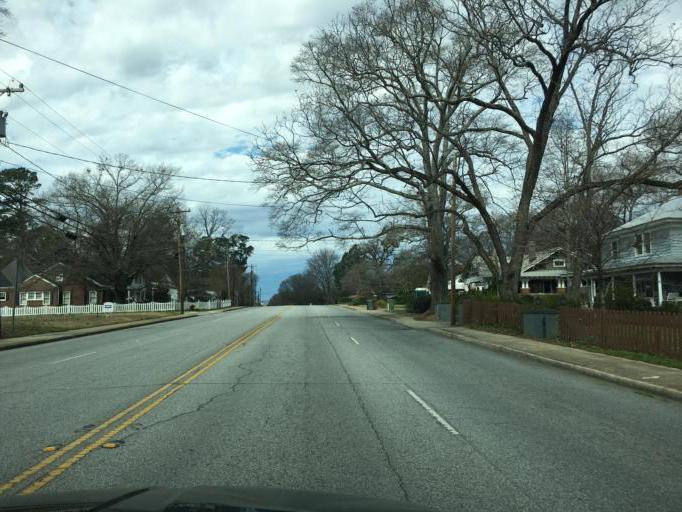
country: US
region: South Carolina
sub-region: Greenville County
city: Fountain Inn
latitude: 34.6972
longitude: -82.2043
